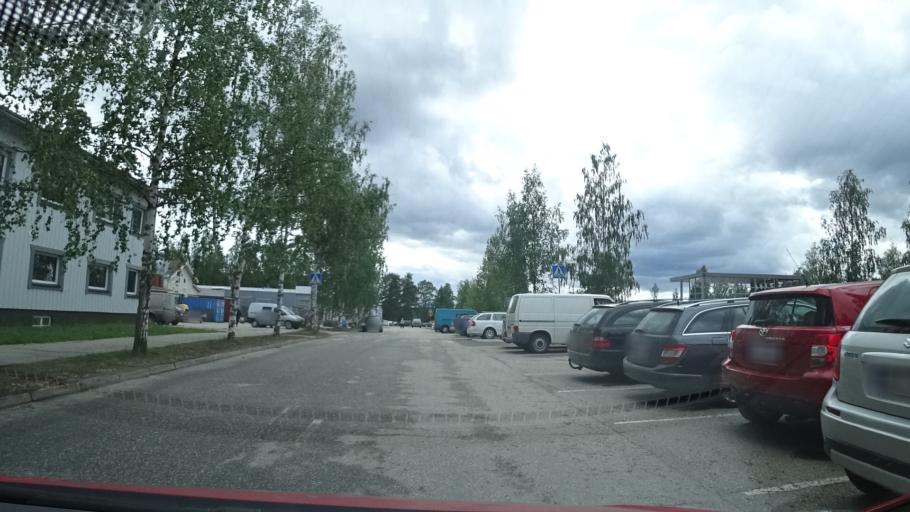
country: FI
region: North Karelia
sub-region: Pielisen Karjala
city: Nurmes
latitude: 63.5427
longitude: 29.1421
